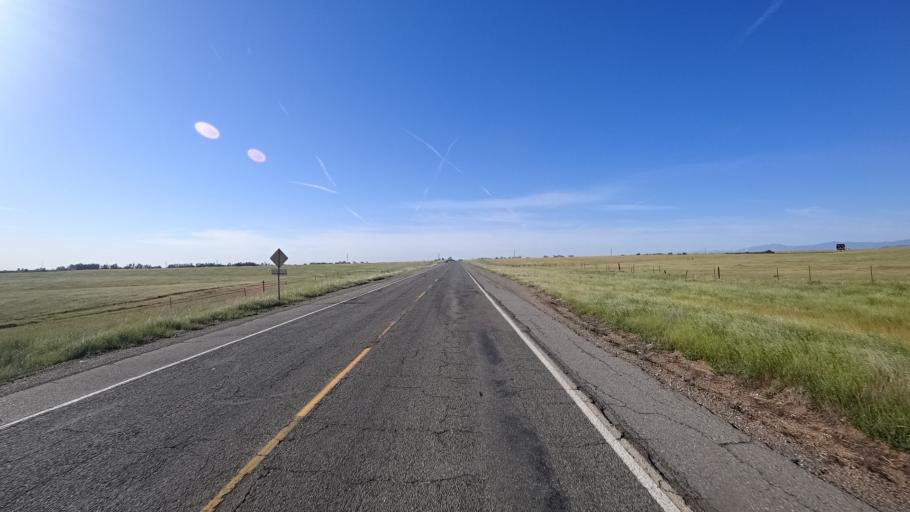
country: US
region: California
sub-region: Glenn County
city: Orland
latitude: 39.8111
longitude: -122.1973
